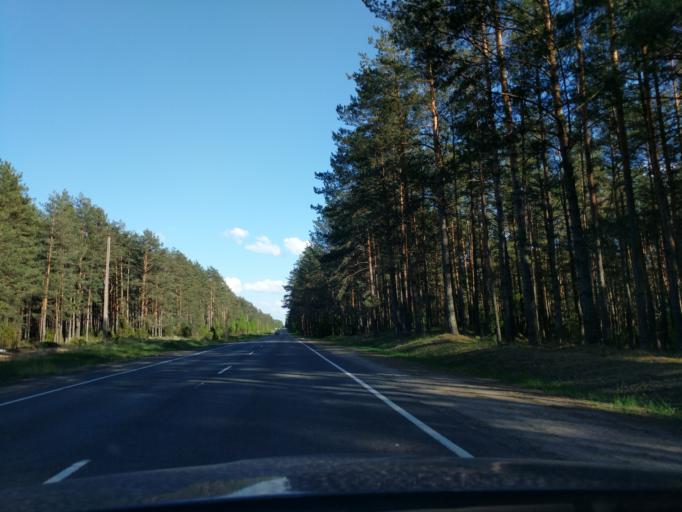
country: BY
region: Minsk
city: Myadzyel
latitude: 54.8223
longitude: 26.9547
